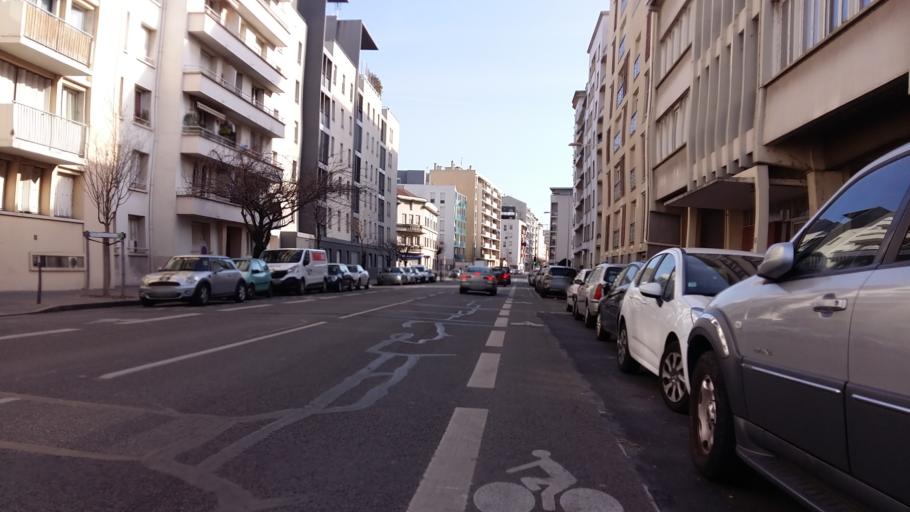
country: FR
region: Rhone-Alpes
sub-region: Departement du Rhone
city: Lyon
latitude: 45.7348
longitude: 4.8571
